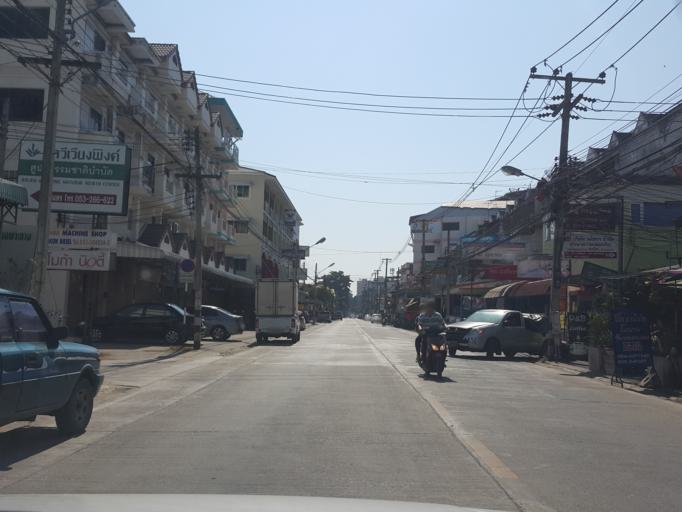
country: TH
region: Chiang Mai
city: Chiang Mai
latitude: 18.7991
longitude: 99.0146
